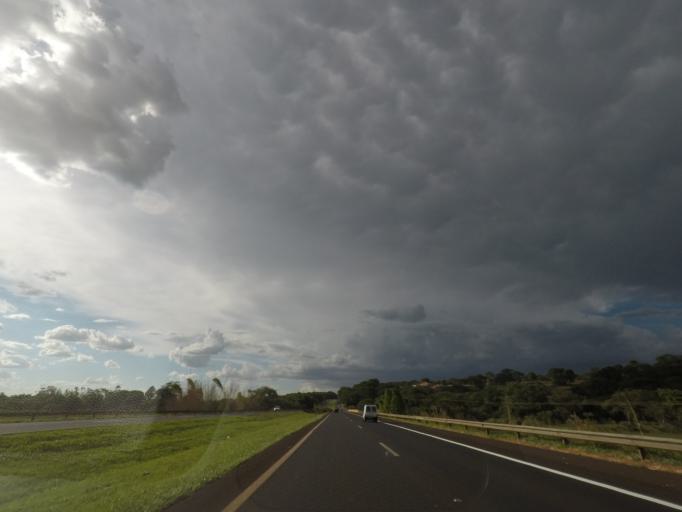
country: BR
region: Sao Paulo
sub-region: Jardinopolis
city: Jardinopolis
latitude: -21.0680
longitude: -47.8134
